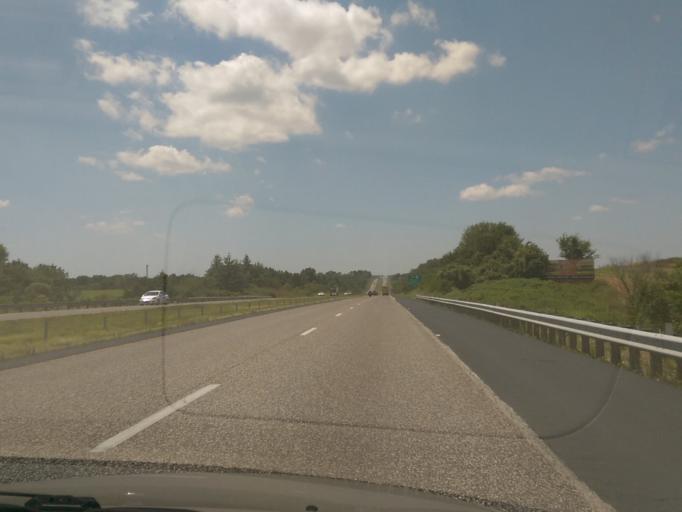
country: US
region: Missouri
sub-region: Cooper County
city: Boonville
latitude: 38.9383
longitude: -92.6657
